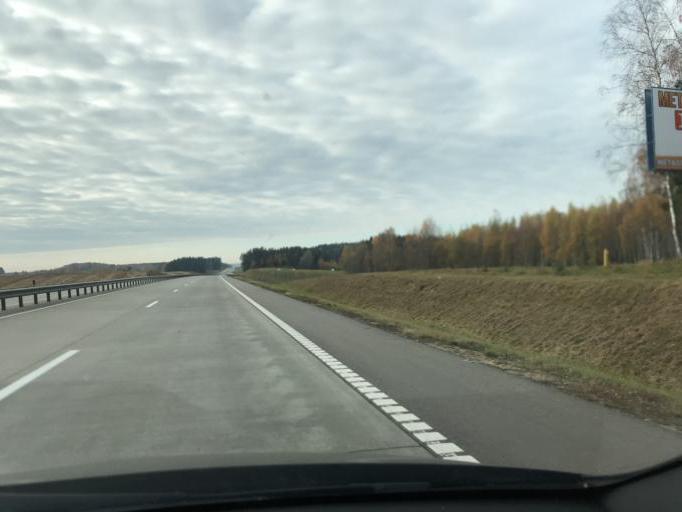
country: BY
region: Minsk
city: Rakaw
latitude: 54.0107
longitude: 27.1332
